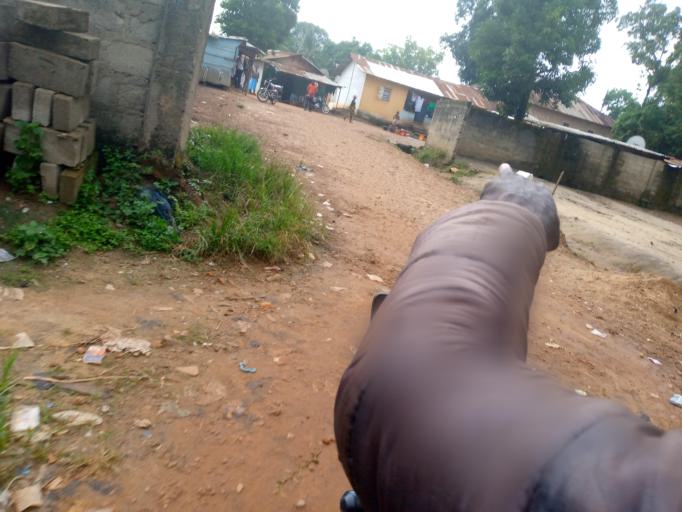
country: SL
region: Eastern Province
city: Kenema
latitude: 7.8760
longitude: -11.1795
